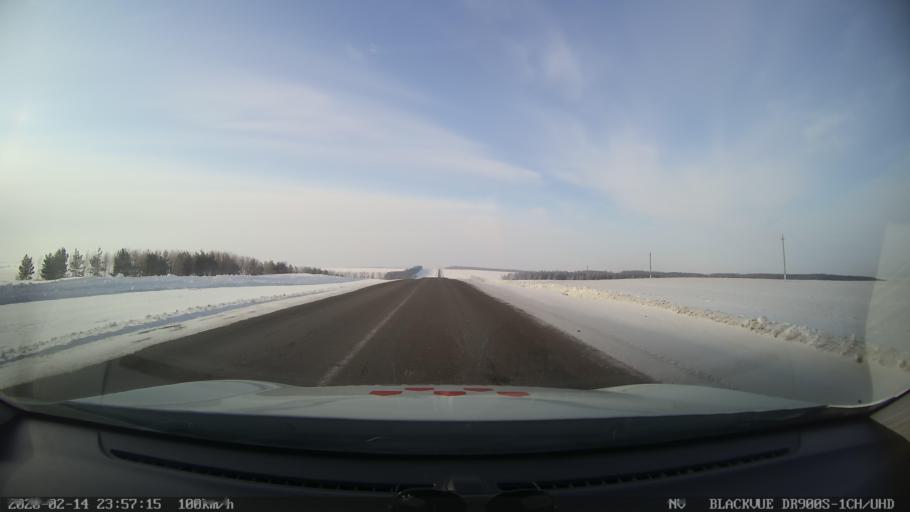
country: RU
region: Tatarstan
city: Kuybyshevskiy Zaton
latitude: 55.3324
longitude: 49.1143
